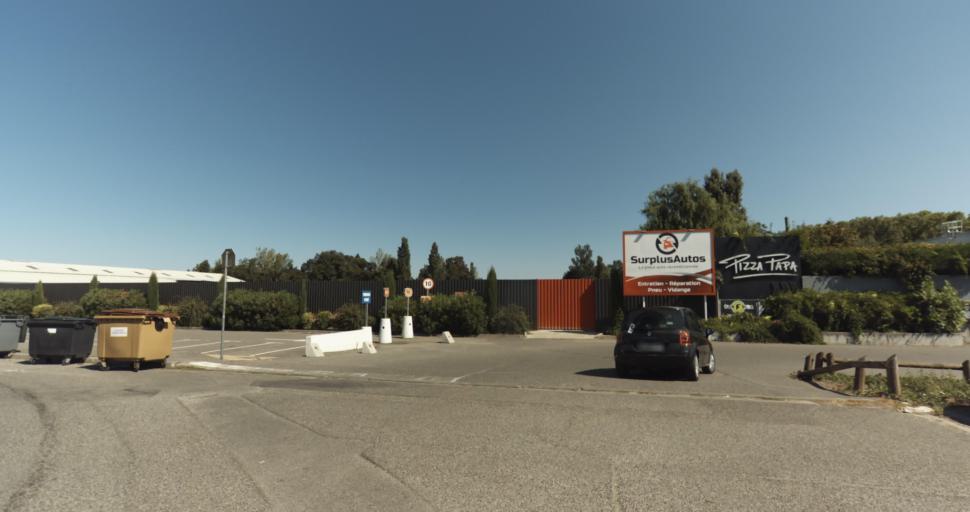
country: FR
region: Midi-Pyrenees
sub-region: Departement de la Haute-Garonne
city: Montrabe
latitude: 43.6407
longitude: 1.5025
